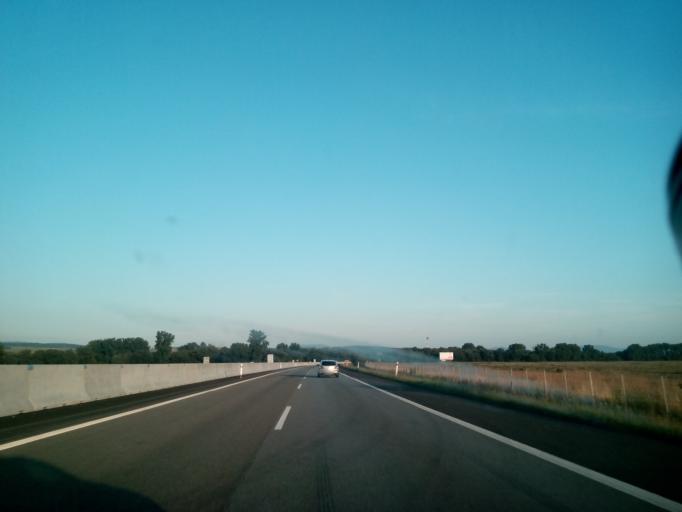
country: SK
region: Kosicky
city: Kosice
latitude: 48.8449
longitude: 21.2931
